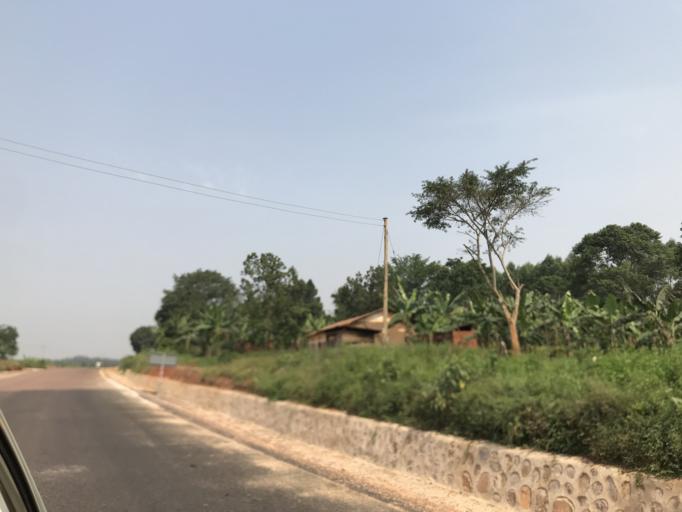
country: UG
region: Central Region
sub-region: Kalungu District
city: Kalungu
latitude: -0.2283
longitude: 31.7230
